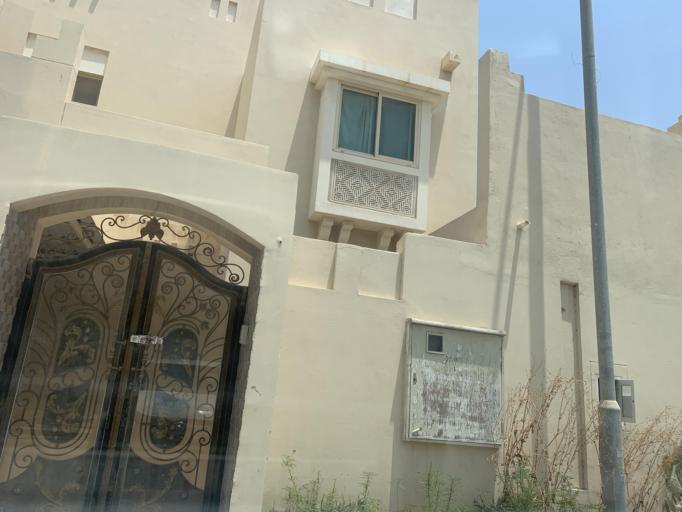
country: BH
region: Manama
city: Jidd Hafs
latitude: 26.2087
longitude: 50.4722
